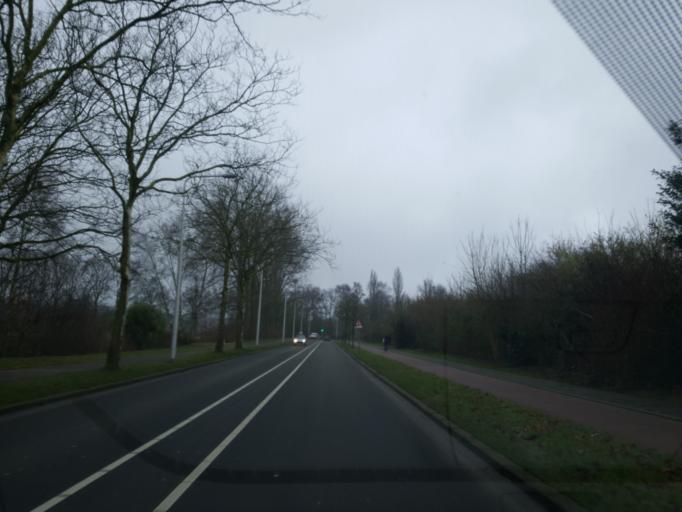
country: NL
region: North Holland
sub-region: Gemeente Bussum
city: Bussum
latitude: 52.2702
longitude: 5.1409
